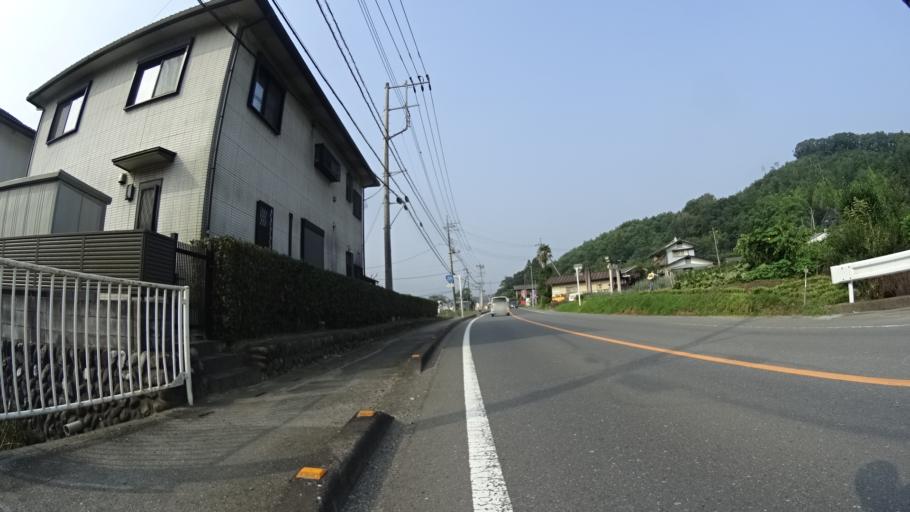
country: JP
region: Saitama
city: Chichibu
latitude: 36.0207
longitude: 139.0658
